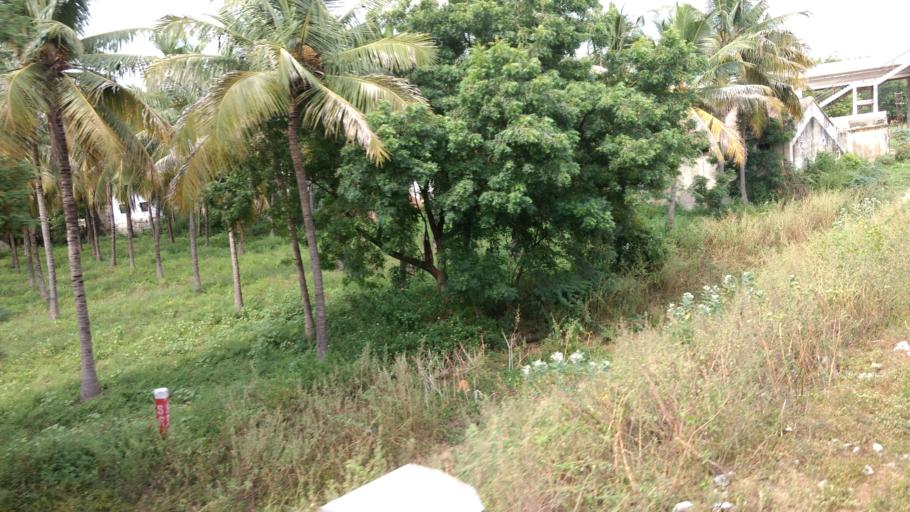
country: IN
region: Tamil Nadu
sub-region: Vellore
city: Gudiyatham
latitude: 12.9365
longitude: 78.9107
